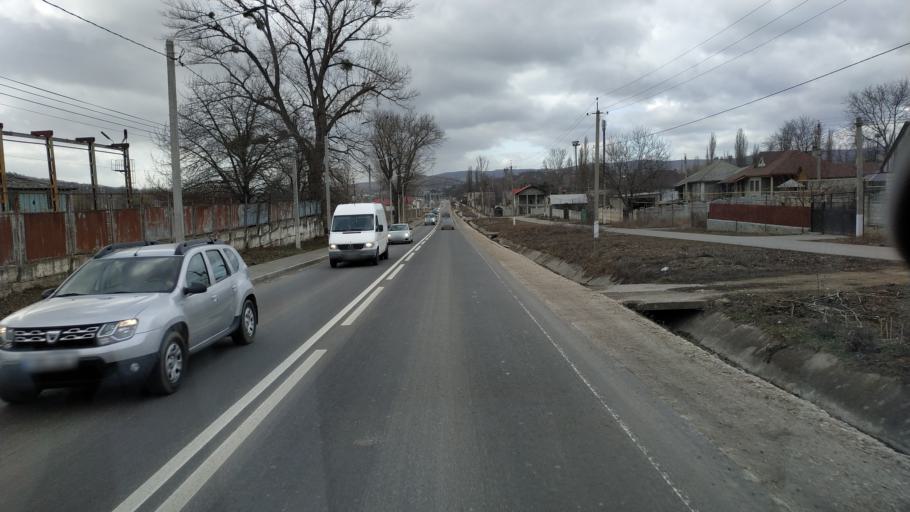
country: MD
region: Calarasi
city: Calarasi
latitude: 47.2780
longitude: 28.2128
